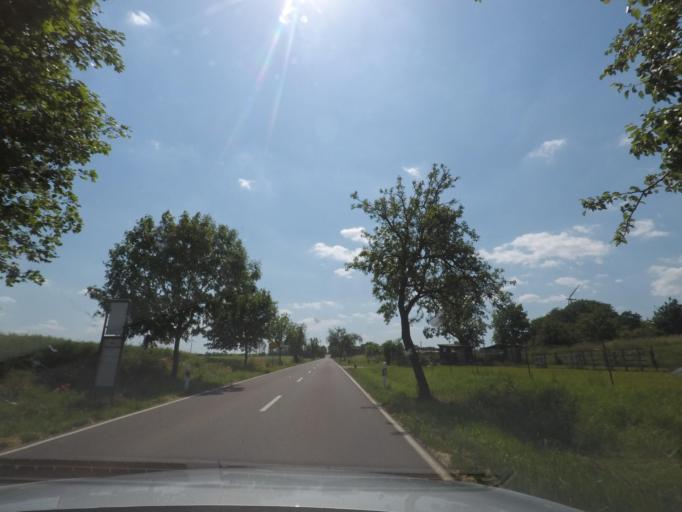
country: DE
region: Saxony-Anhalt
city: Eichenbarleben
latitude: 52.2103
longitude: 11.3947
